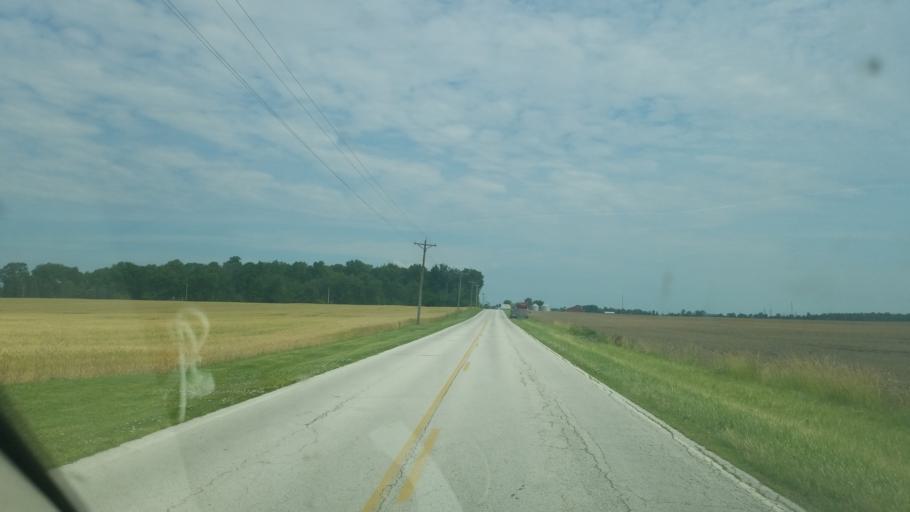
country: US
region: Ohio
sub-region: Seneca County
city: Fostoria
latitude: 41.1048
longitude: -83.4785
